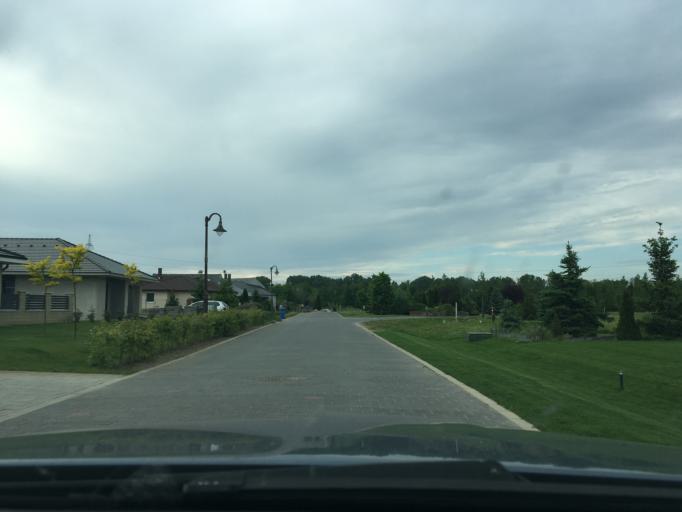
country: HU
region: Hajdu-Bihar
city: Debrecen
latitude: 47.5517
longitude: 21.6896
